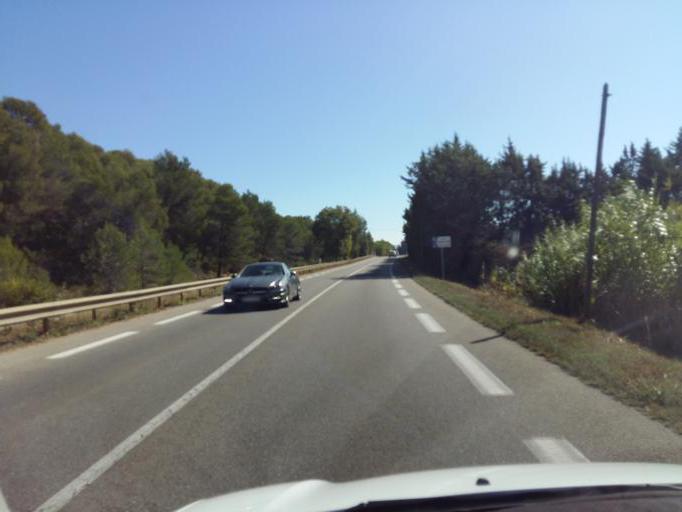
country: FR
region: Provence-Alpes-Cote d'Azur
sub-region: Departement des Bouches-du-Rhone
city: Senas
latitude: 43.7677
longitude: 5.1239
